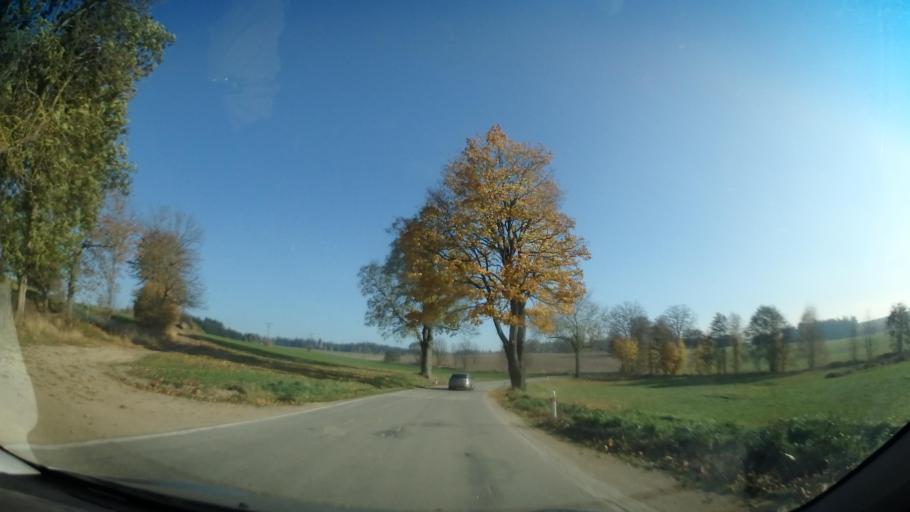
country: CZ
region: Vysocina
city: Zd'ar nad Sazavou Druhy
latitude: 49.6109
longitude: 15.9220
